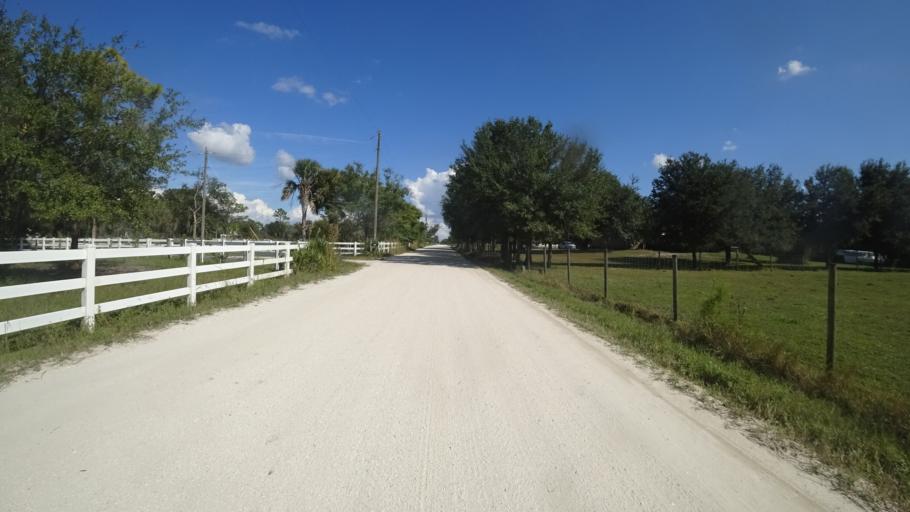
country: US
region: Florida
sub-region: Sarasota County
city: The Meadows
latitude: 27.4526
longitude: -82.2964
